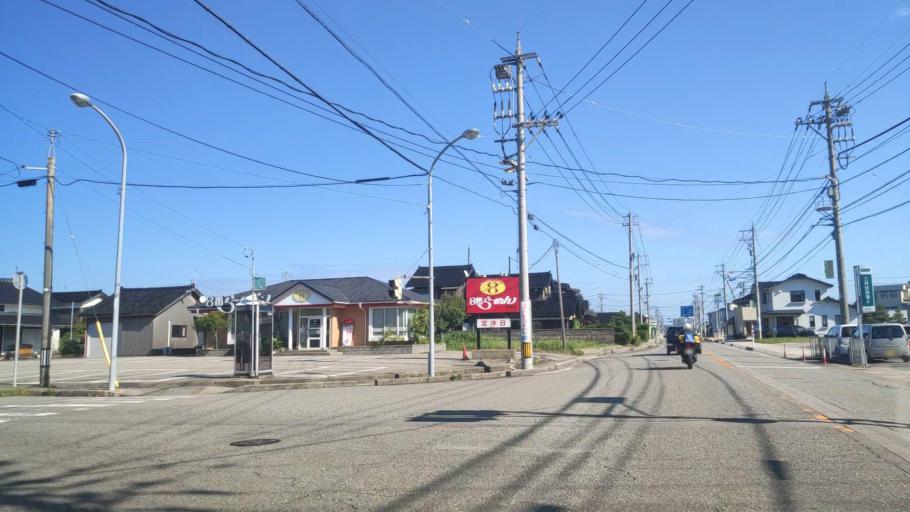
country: JP
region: Ishikawa
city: Hakui
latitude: 36.9963
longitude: 136.7769
